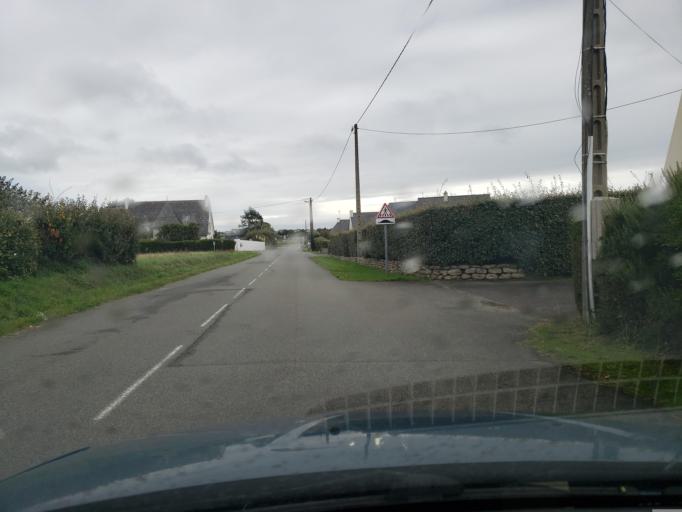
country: FR
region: Brittany
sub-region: Departement du Finistere
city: Guilvinec
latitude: 47.8060
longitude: -4.3051
